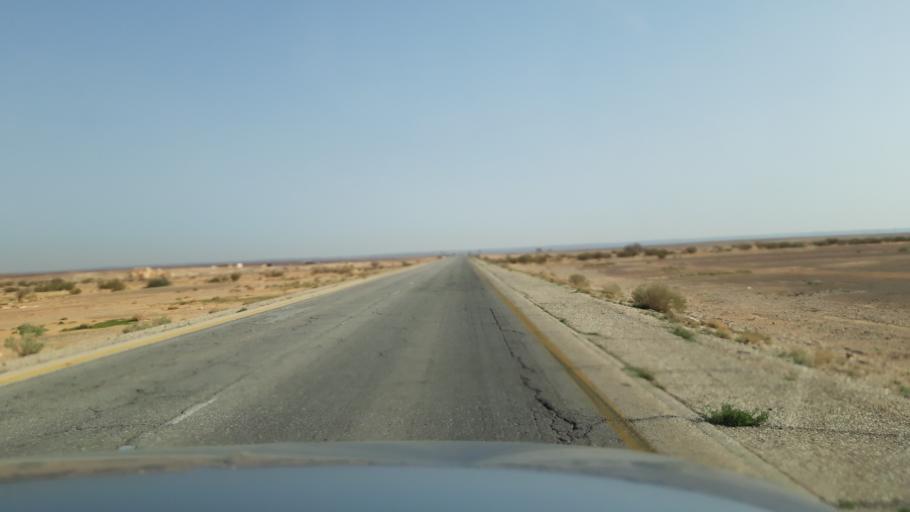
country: JO
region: Amman
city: Al Azraq ash Shamali
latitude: 31.7972
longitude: 36.5869
